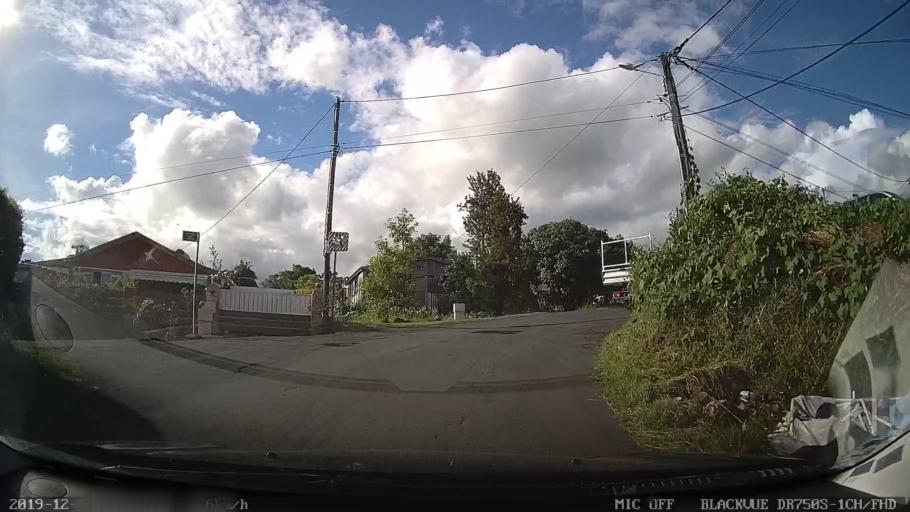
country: RE
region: Reunion
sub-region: Reunion
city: Le Tampon
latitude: -21.2567
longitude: 55.5082
